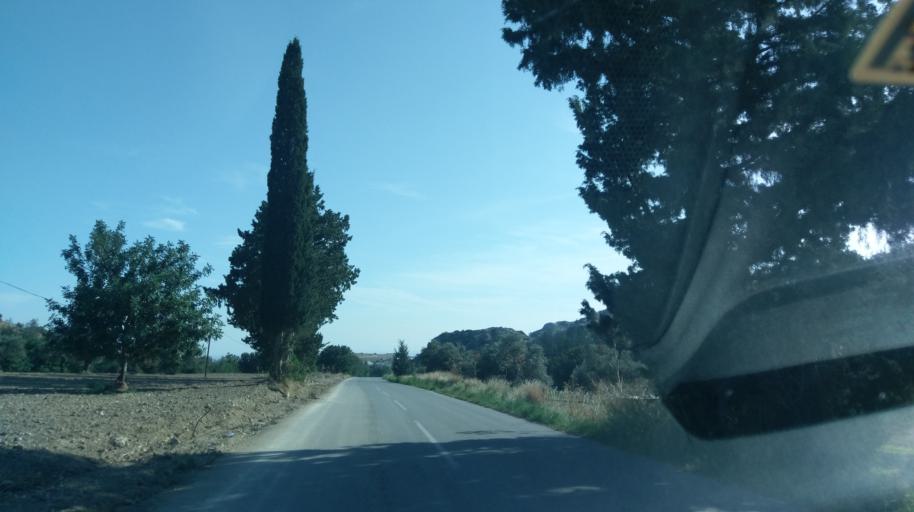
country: CY
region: Ammochostos
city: Trikomo
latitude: 35.3353
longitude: 33.8084
